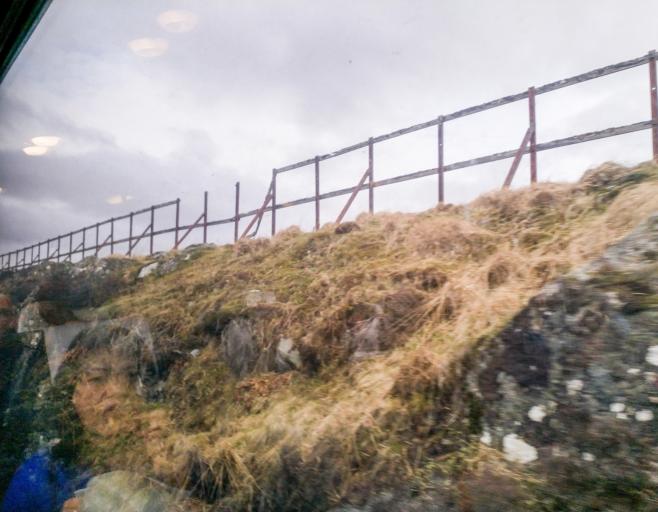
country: GB
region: Scotland
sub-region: Highland
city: Spean Bridge
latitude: 56.7023
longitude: -4.5820
